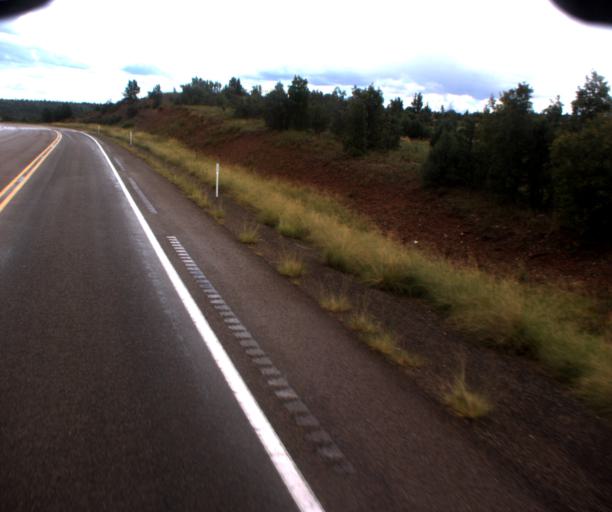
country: US
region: Arizona
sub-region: Navajo County
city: Heber-Overgaard
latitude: 34.3665
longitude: -110.4218
